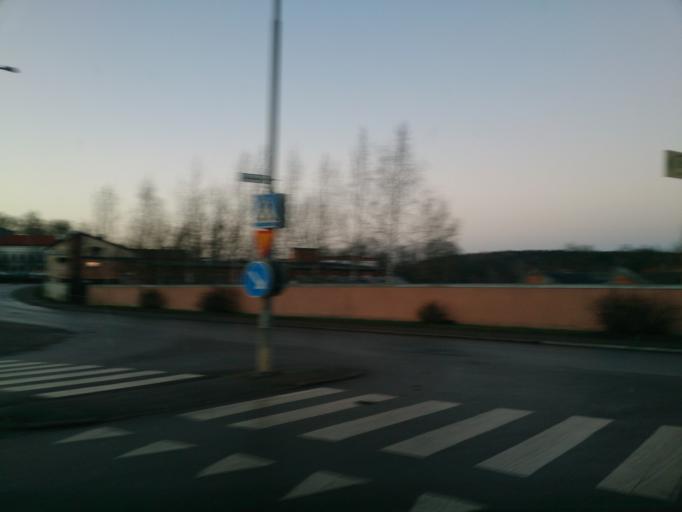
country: SE
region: OEstergoetland
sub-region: Atvidabergs Kommun
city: Atvidaberg
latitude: 58.1977
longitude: 16.0039
